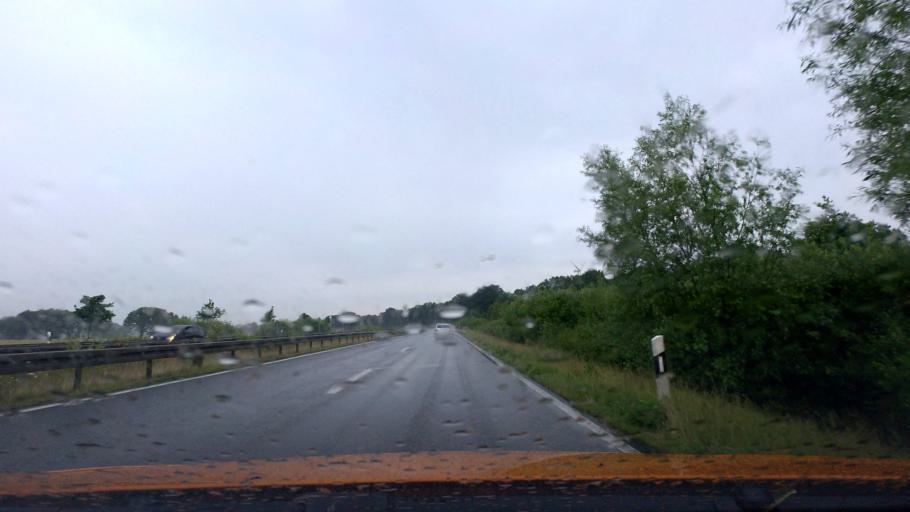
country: DE
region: Lower Saxony
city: Linsburg
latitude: 52.5834
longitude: 9.2863
